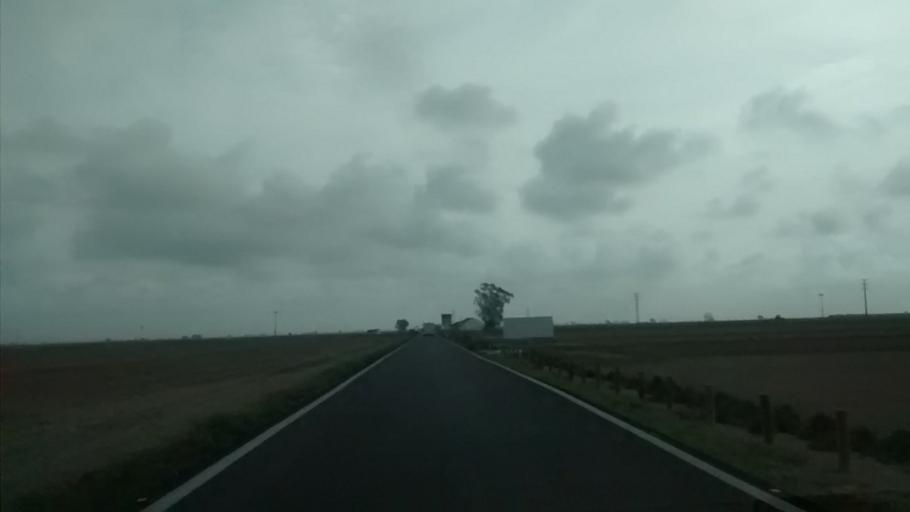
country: ES
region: Catalonia
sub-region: Provincia de Tarragona
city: Deltebre
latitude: 40.6741
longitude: 0.6563
